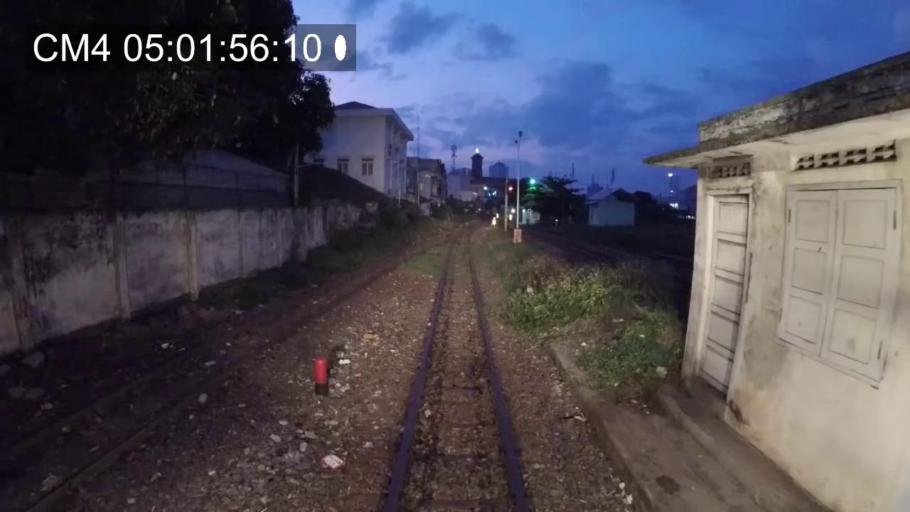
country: VN
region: Khanh Hoa
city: Nha Trang
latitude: 12.2496
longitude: 109.1803
